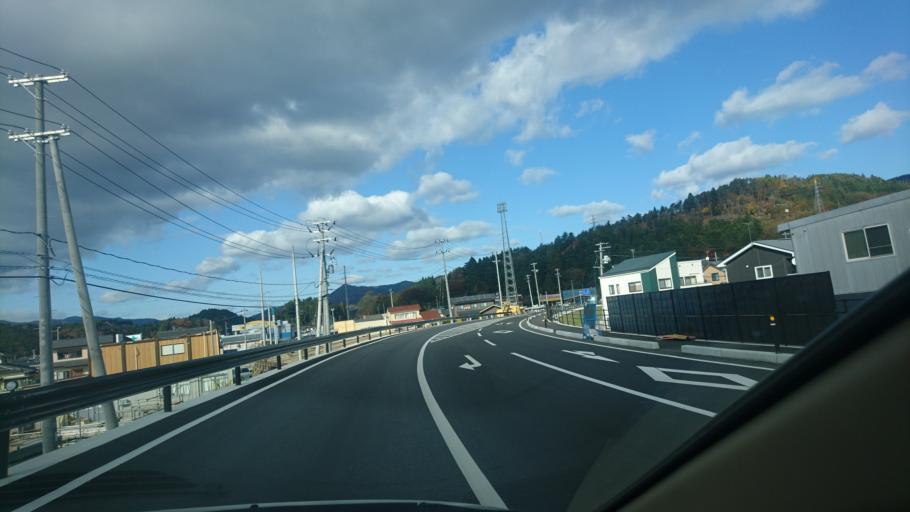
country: JP
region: Iwate
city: Ofunato
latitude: 38.9182
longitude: 141.5867
